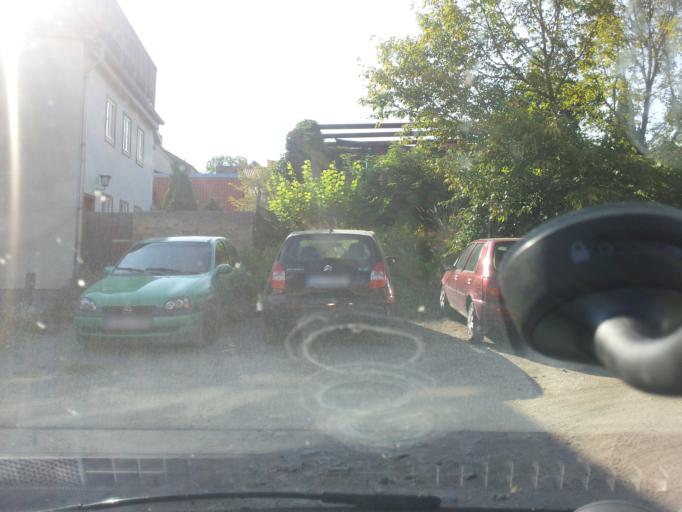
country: DE
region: Saxony-Anhalt
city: Quedlinburg
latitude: 51.7918
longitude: 11.1425
